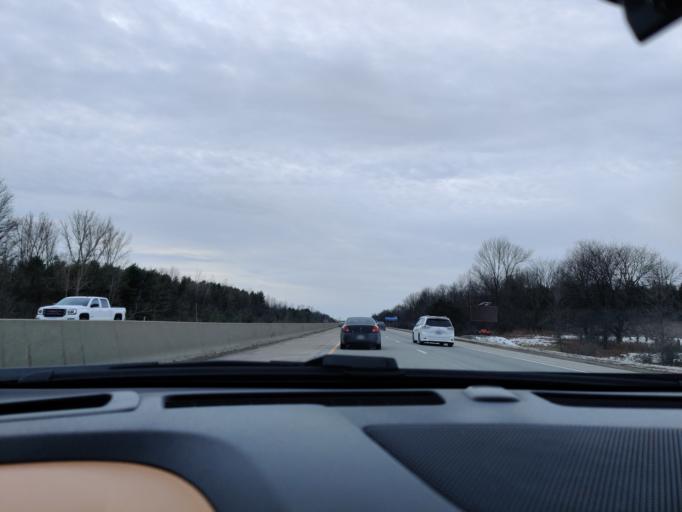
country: CA
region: Ontario
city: Brockville
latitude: 44.6309
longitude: -75.6545
